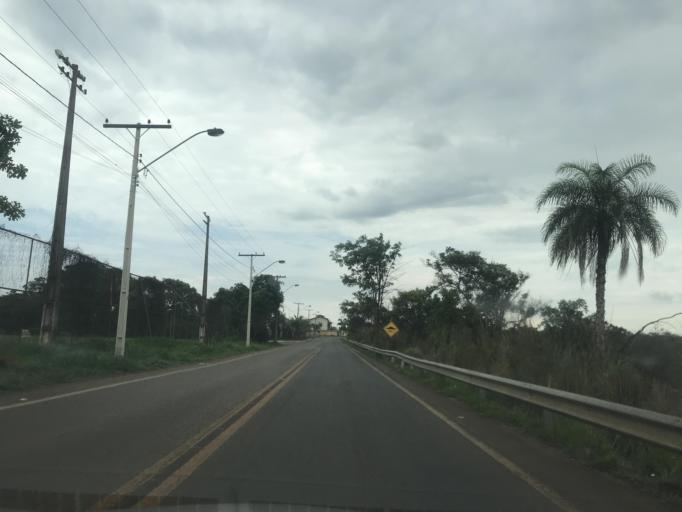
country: BR
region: Goias
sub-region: Luziania
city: Luziania
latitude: -16.2575
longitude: -47.9723
